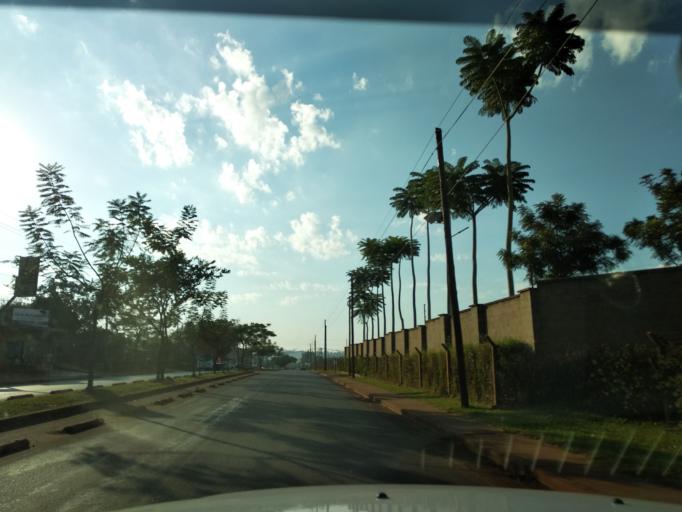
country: AR
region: Misiones
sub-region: Departamento de Capital
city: Posadas
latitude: -27.4275
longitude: -55.9169
